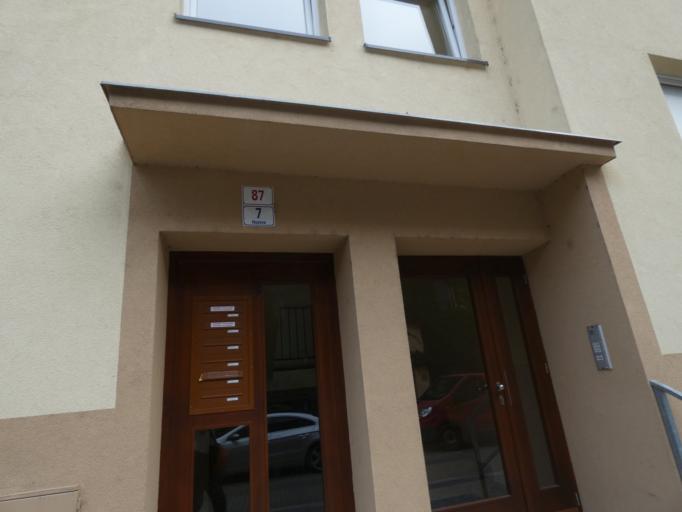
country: CZ
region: South Moravian
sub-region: Okres Breclav
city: Mikulov
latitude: 48.8081
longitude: 16.6363
